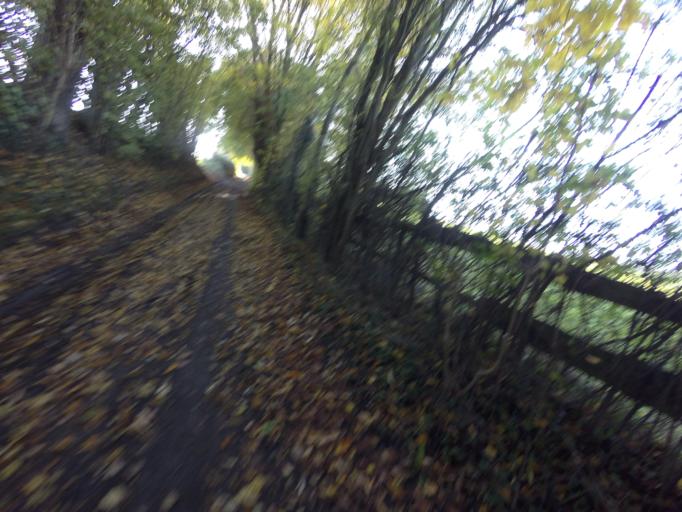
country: NL
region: Limburg
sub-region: Eijsden-Margraten
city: Margraten
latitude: 50.7963
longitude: 5.8683
